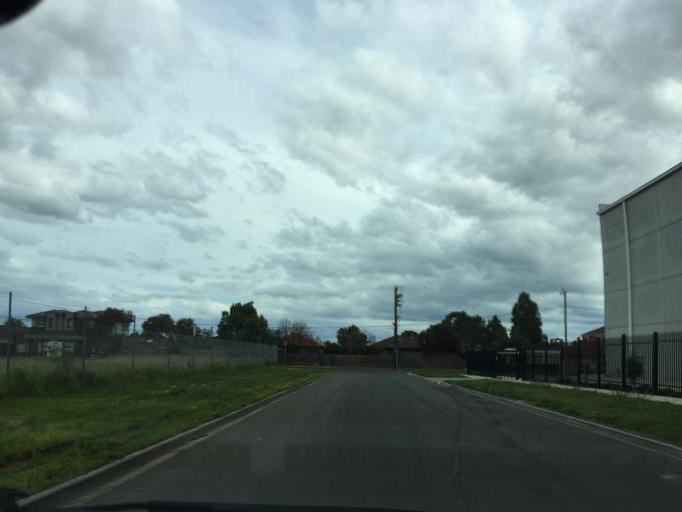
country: AU
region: Victoria
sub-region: Maribyrnong
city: West Footscray
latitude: -37.8032
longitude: 144.8689
